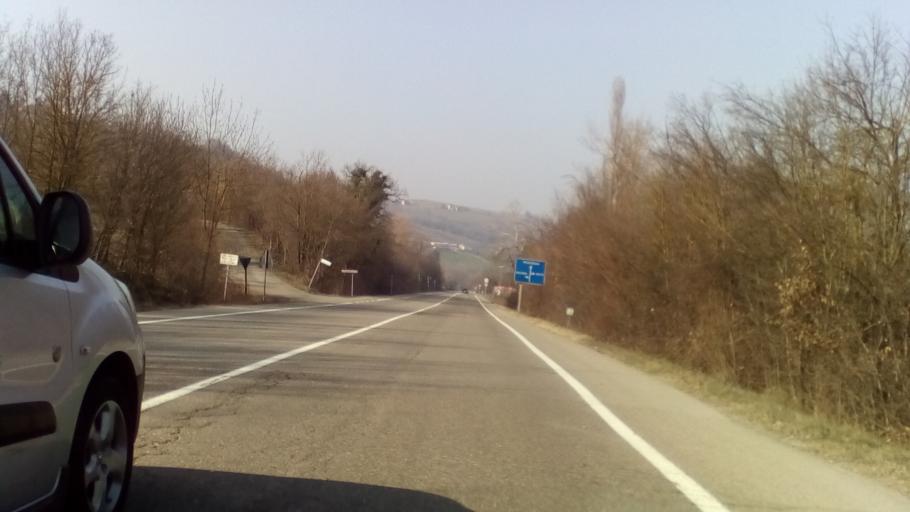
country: IT
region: Emilia-Romagna
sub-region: Provincia di Modena
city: Serramazzoni
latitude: 44.4279
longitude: 10.8420
